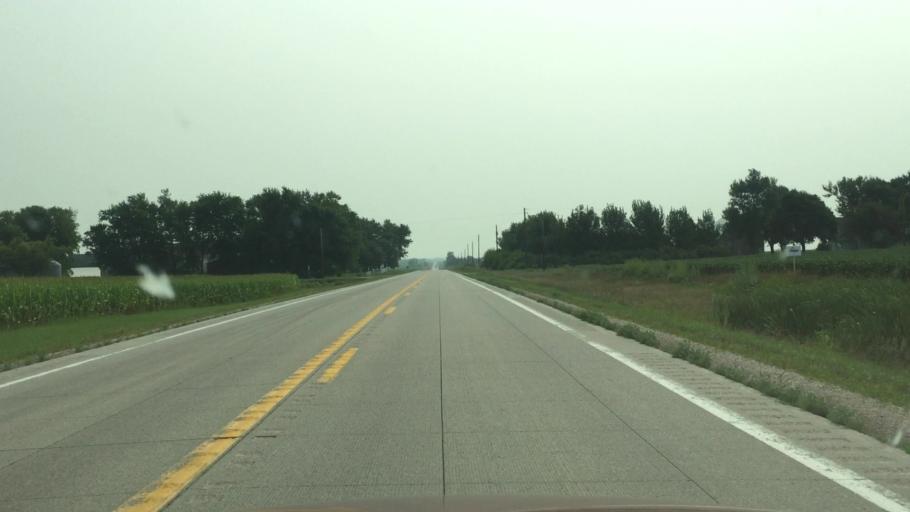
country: US
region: Iowa
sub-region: Osceola County
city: Sibley
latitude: 43.4326
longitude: -95.6646
